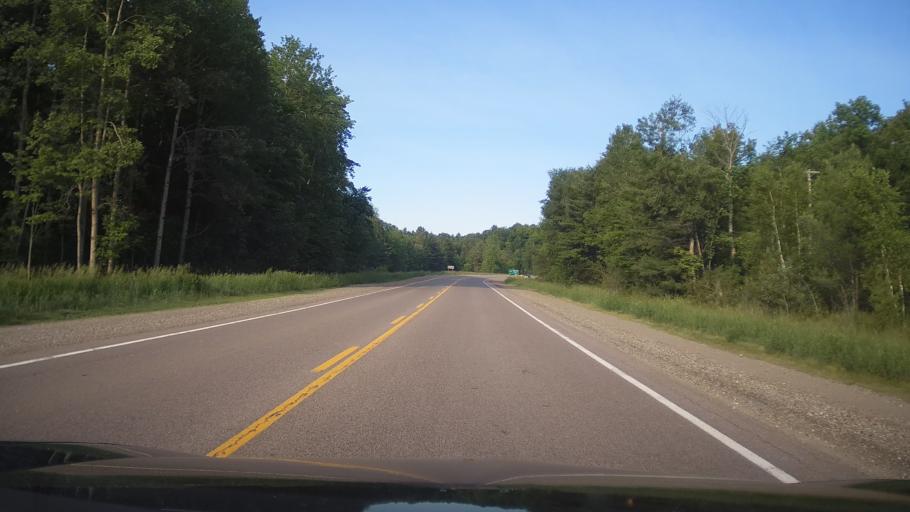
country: CA
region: Ontario
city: Skatepark
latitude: 44.7243
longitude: -76.9692
